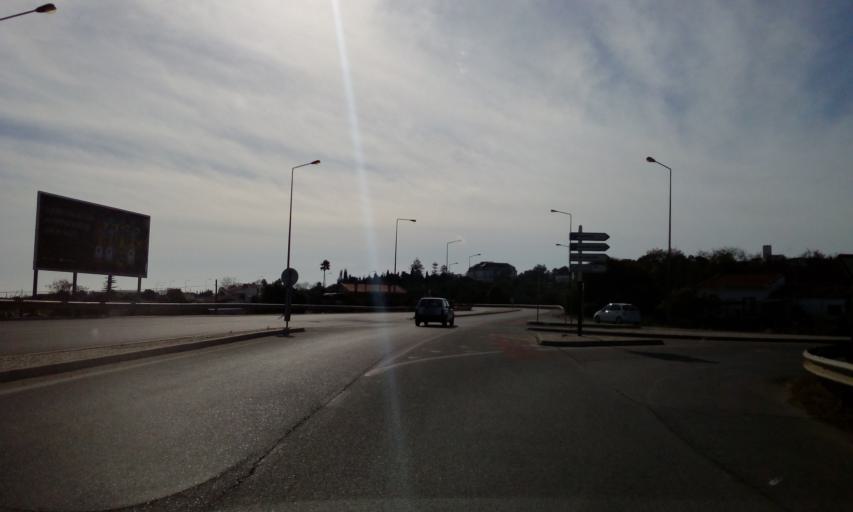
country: PT
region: Faro
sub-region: Faro
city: Faro
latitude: 37.0254
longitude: -7.9169
